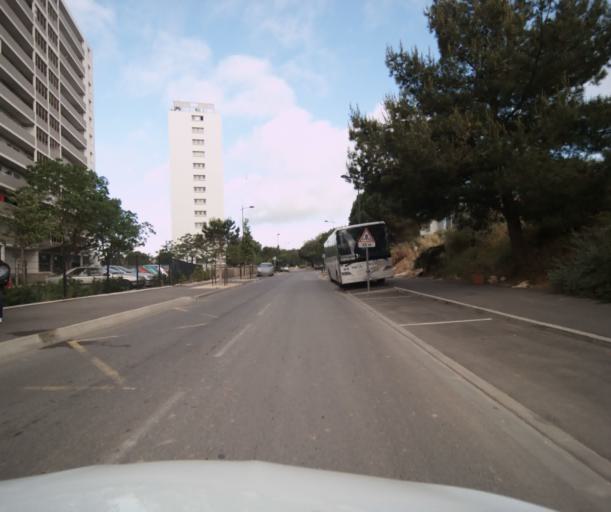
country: FR
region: Provence-Alpes-Cote d'Azur
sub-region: Departement du Var
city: Six-Fours-les-Plages
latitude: 43.1147
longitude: 5.8613
